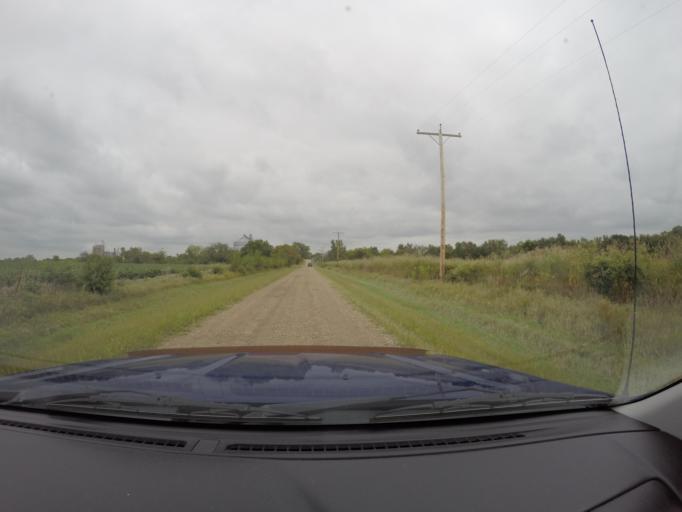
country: US
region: Kansas
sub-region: Morris County
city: Council Grove
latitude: 38.8624
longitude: -96.4965
